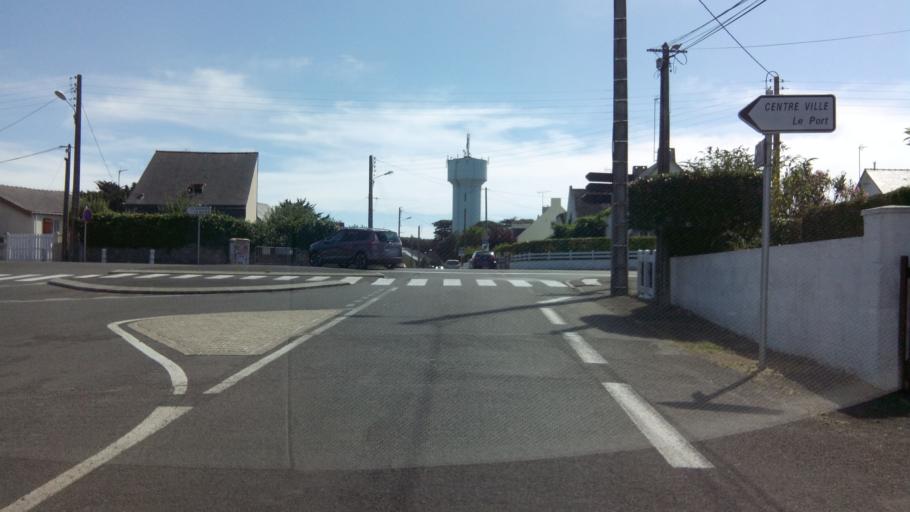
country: FR
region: Pays de la Loire
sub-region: Departement de la Loire-Atlantique
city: Le Croisic
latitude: 47.2921
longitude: -2.5167
